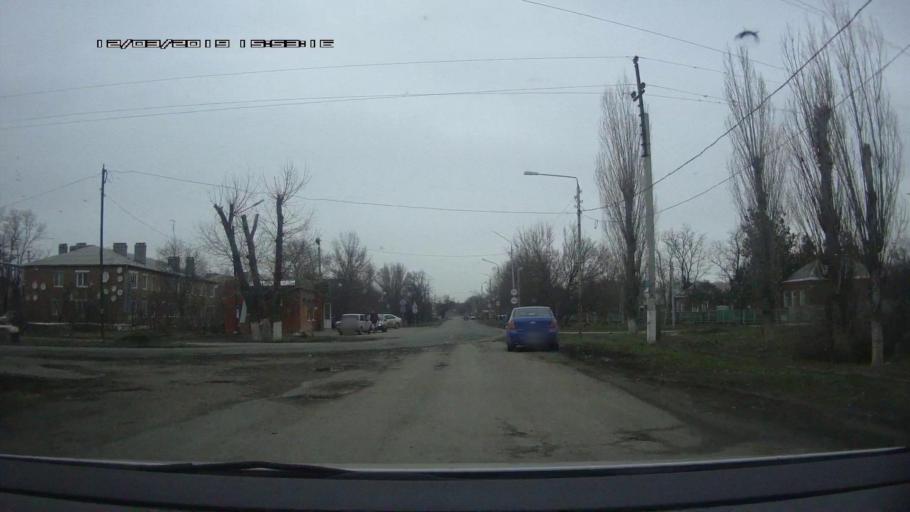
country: RU
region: Rostov
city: Novobataysk
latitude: 46.8845
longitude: 39.7760
